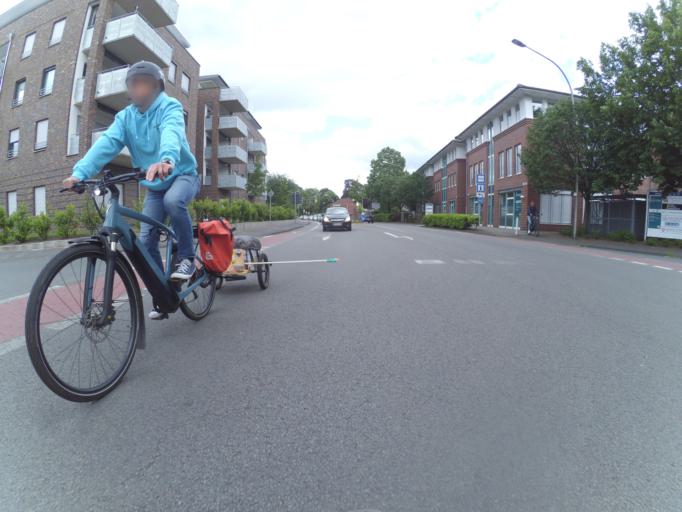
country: DE
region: North Rhine-Westphalia
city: Ibbenburen
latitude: 52.2719
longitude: 7.7156
